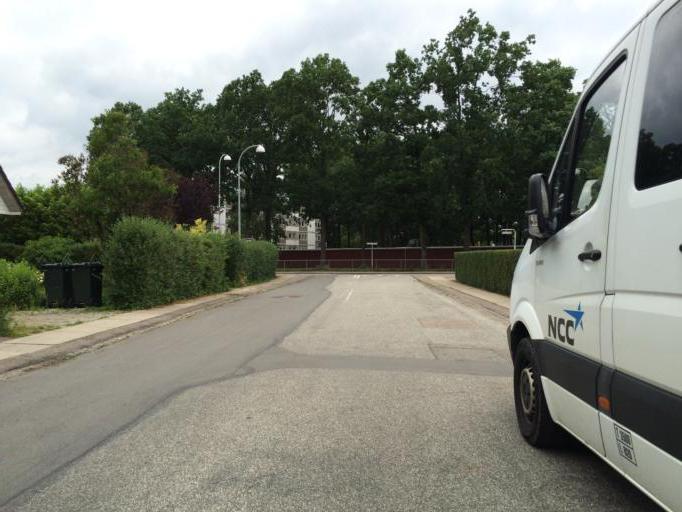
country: DK
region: Capital Region
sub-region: Hvidovre Kommune
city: Hvidovre
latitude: 55.6225
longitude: 12.4803
